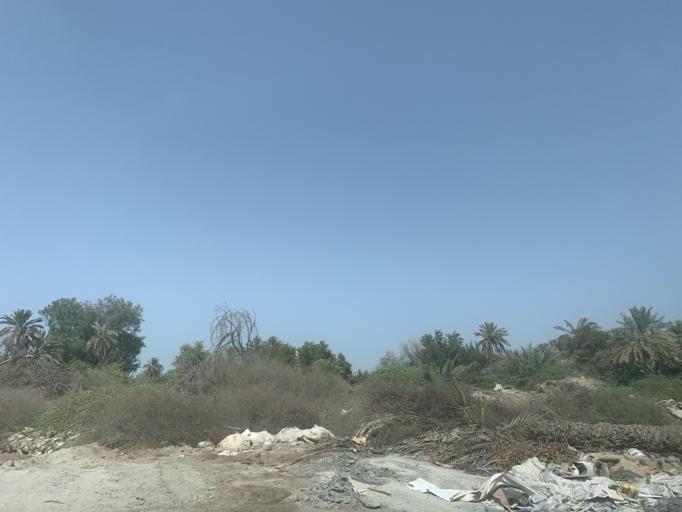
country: BH
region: Manama
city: Jidd Hafs
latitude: 26.2333
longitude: 50.5110
